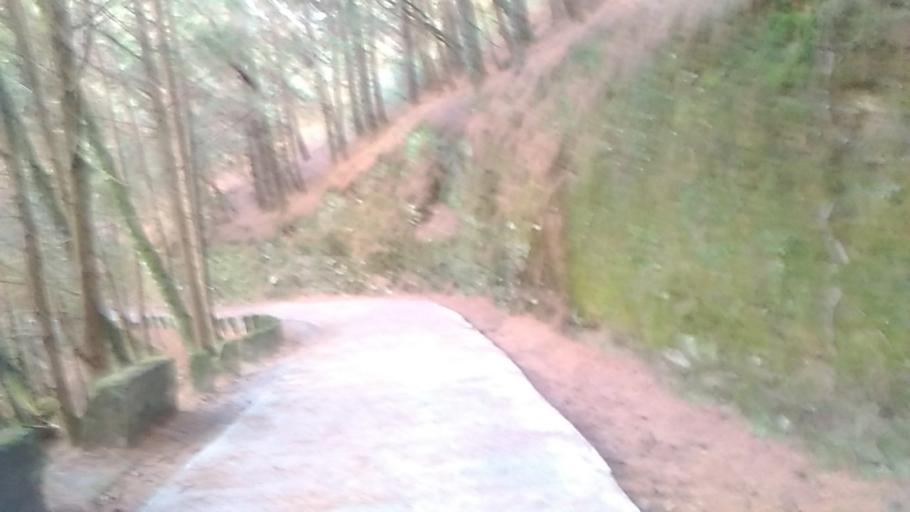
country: TW
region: Taiwan
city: Daxi
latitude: 24.4019
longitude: 121.3070
